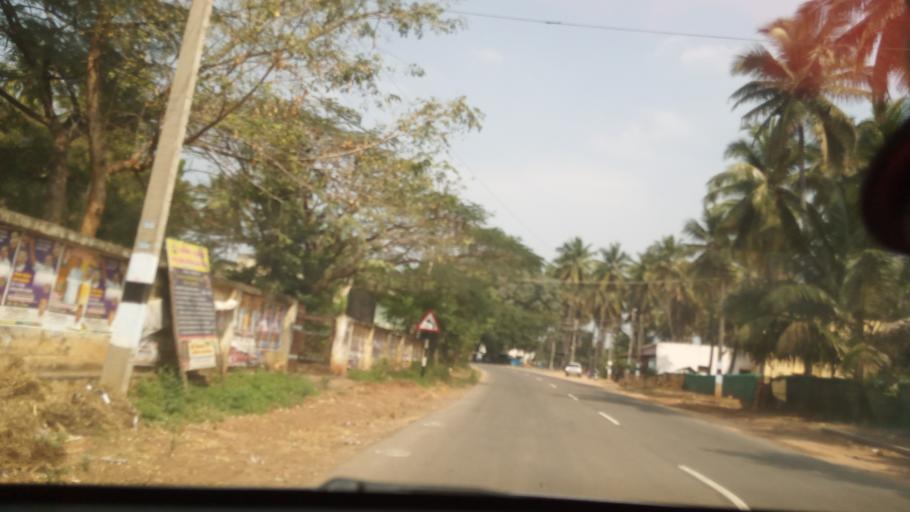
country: IN
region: Tamil Nadu
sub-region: Coimbatore
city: Perur
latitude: 10.9982
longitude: 76.8515
